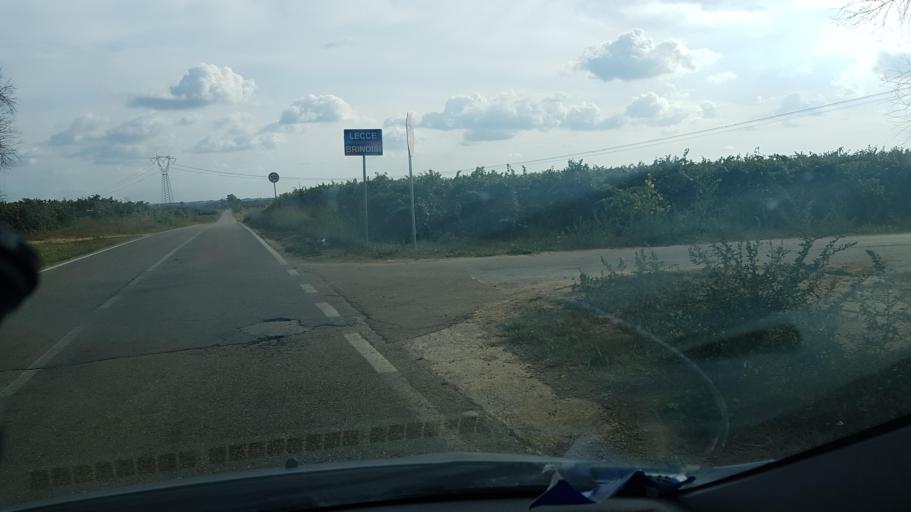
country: IT
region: Apulia
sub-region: Provincia di Brindisi
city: Cellino San Marco
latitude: 40.4570
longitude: 17.9555
